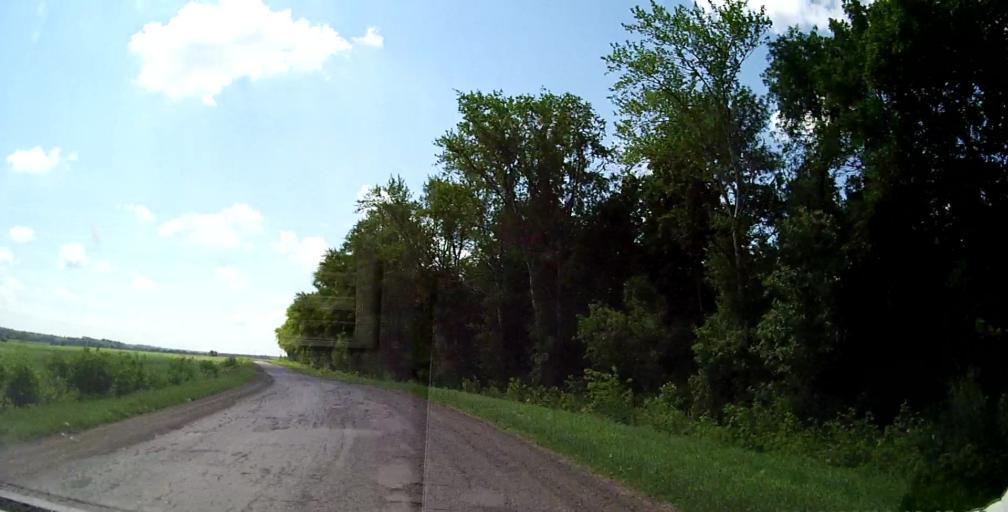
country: RU
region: Lipetsk
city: Chaplygin
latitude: 53.3003
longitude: 39.9521
